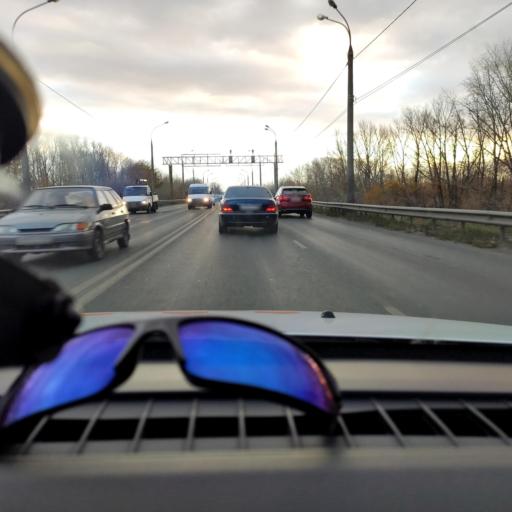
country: RU
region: Samara
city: Samara
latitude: 53.1502
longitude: 50.1861
